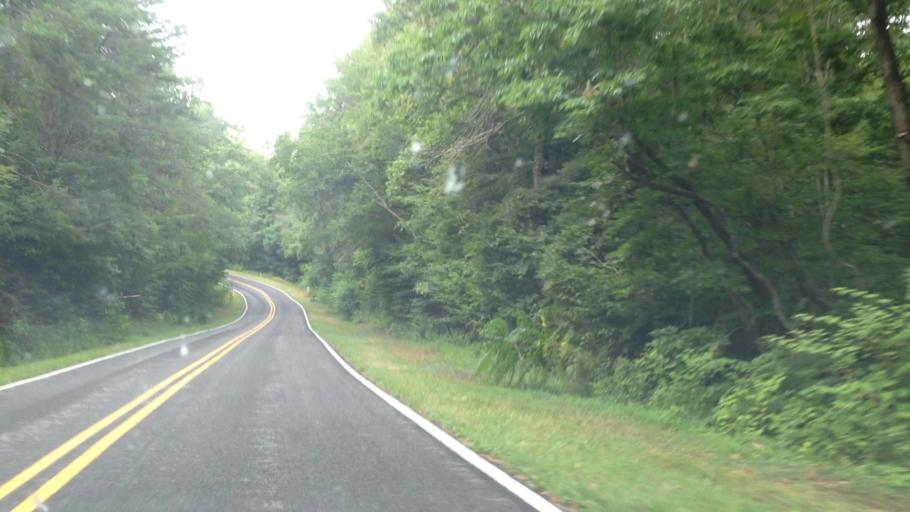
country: US
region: North Carolina
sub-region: Rockingham County
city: Mayodan
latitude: 36.4297
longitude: -80.0861
